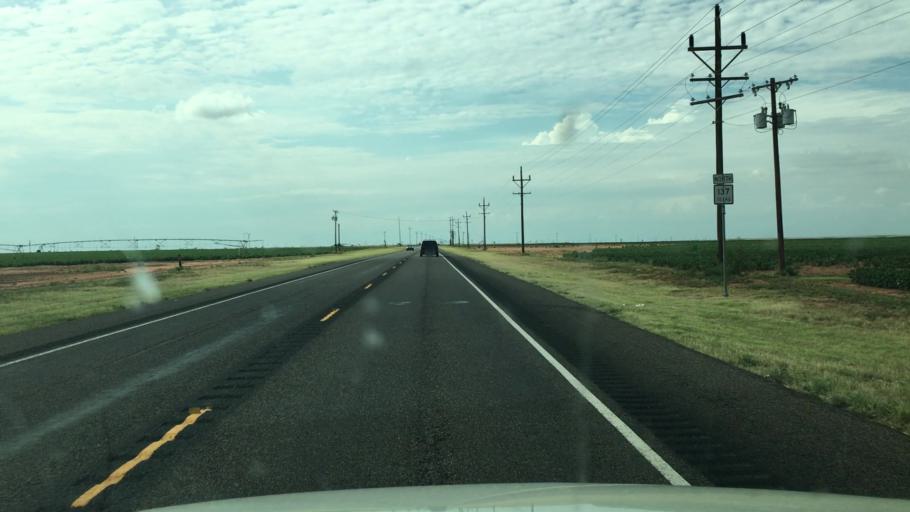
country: US
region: Texas
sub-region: Dawson County
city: Lamesa
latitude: 32.8860
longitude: -102.0856
